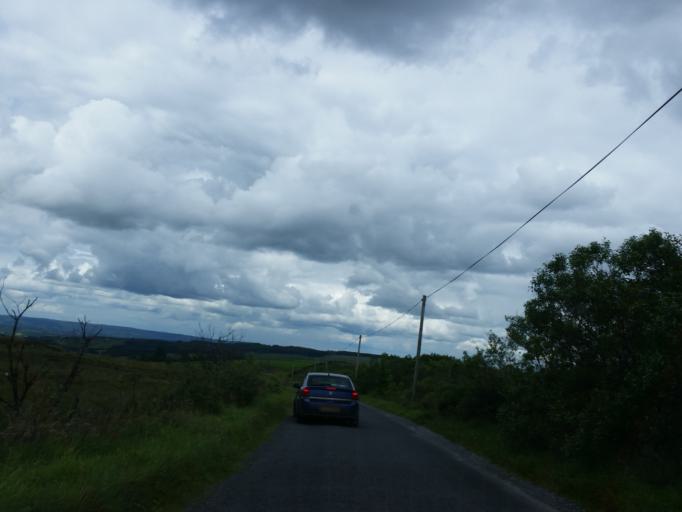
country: IE
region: Ulster
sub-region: County Monaghan
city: Clones
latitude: 54.2701
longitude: -7.2743
